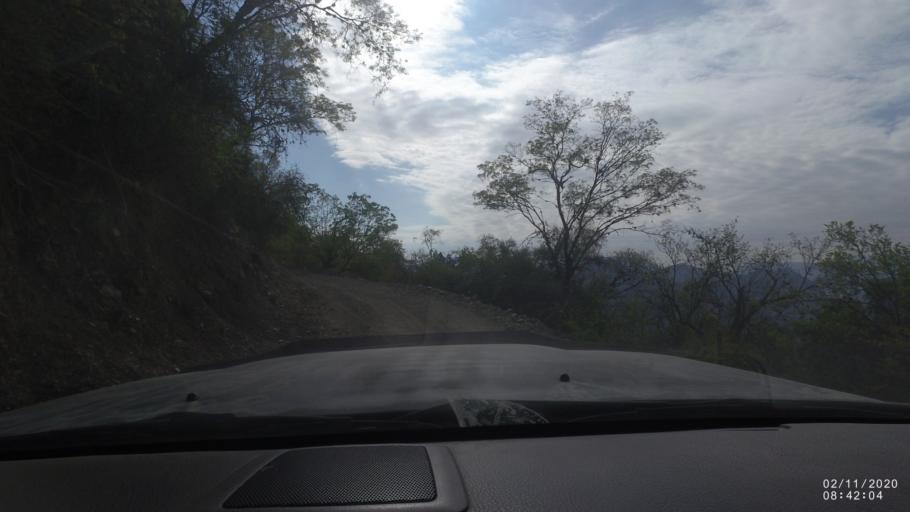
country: BO
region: Chuquisaca
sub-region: Provincia Zudanez
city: Mojocoya
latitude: -18.5768
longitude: -64.5501
